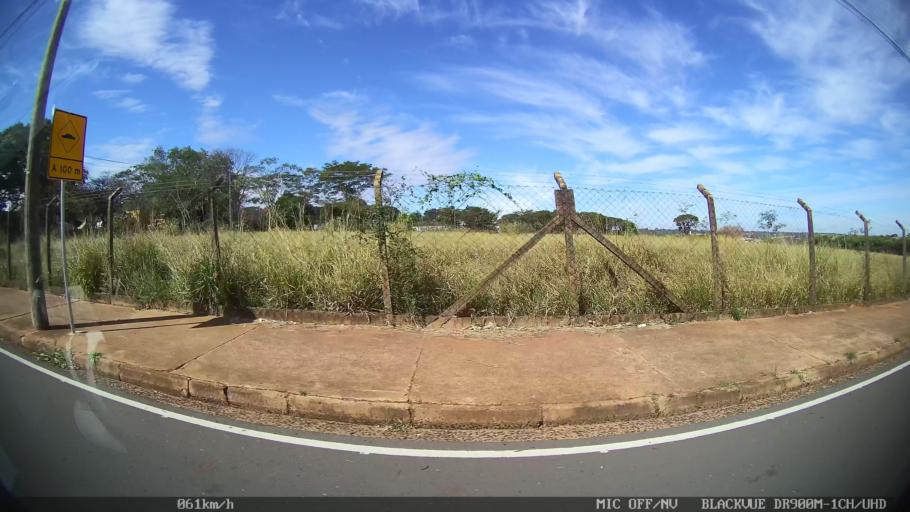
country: BR
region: Sao Paulo
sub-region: Sao Jose Do Rio Preto
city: Sao Jose do Rio Preto
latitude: -20.8355
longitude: -49.3639
